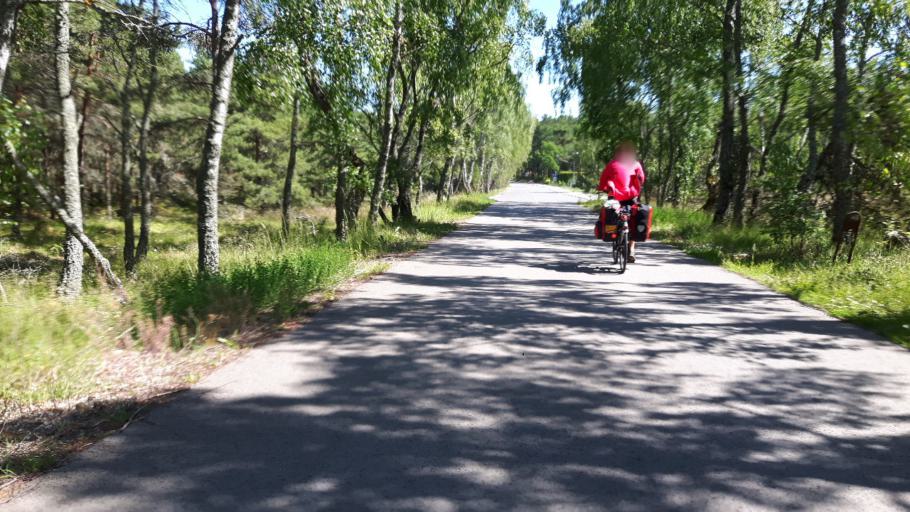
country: LT
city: Neringa
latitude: 55.4117
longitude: 21.0897
